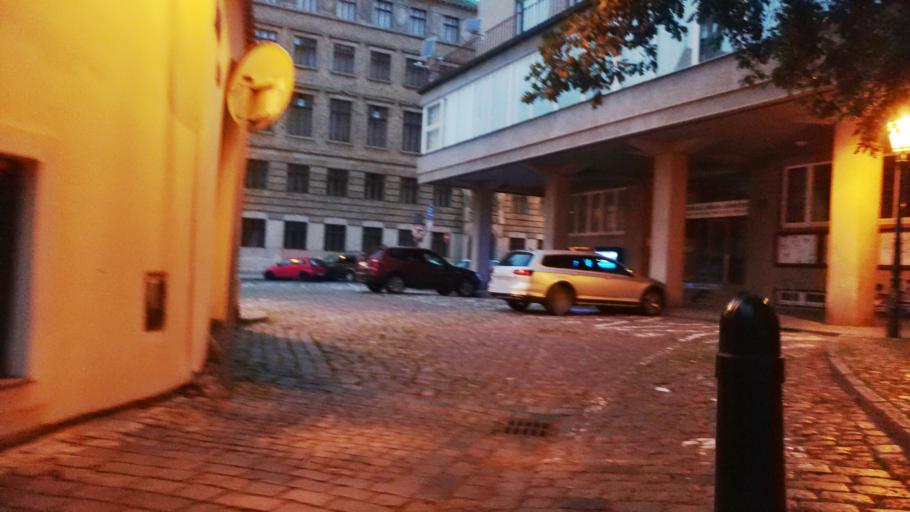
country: CZ
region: Praha
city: Prague
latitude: 50.0921
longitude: 14.4252
